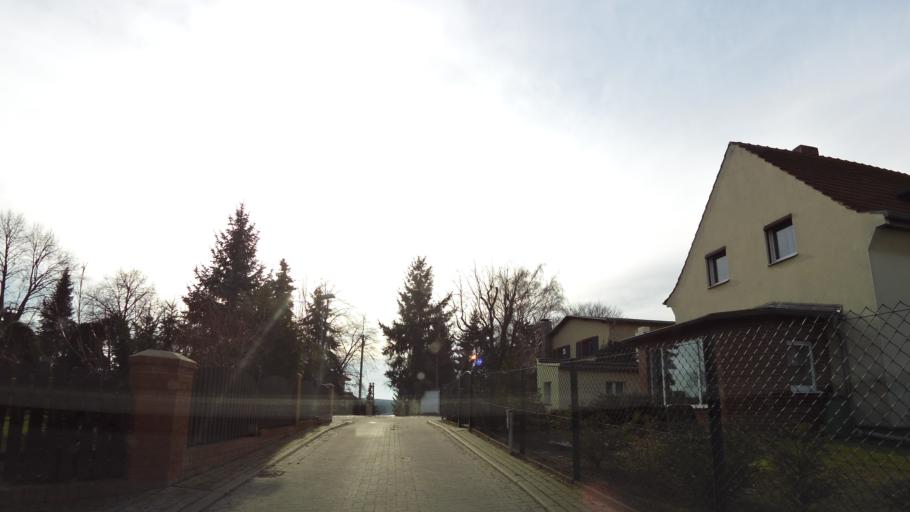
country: DE
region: Brandenburg
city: Michendorf
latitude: 52.3443
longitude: 12.9990
